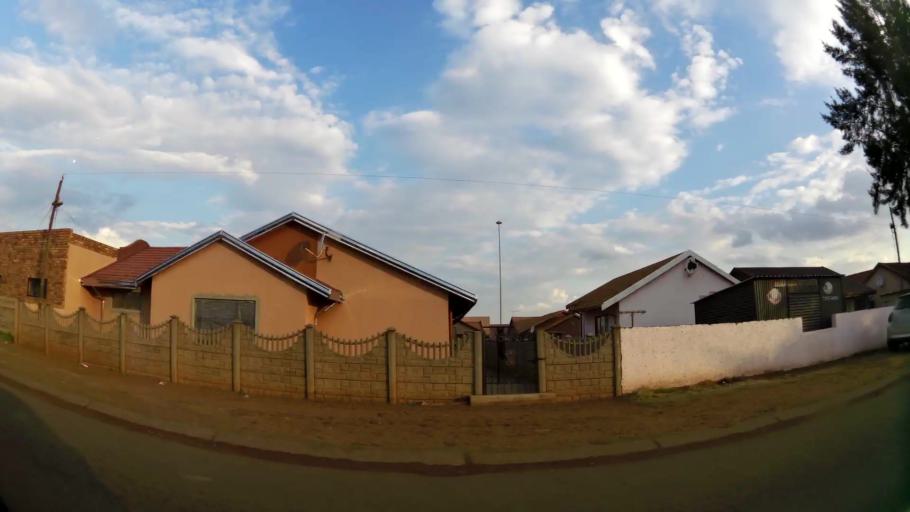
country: ZA
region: Gauteng
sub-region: City of Johannesburg Metropolitan Municipality
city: Orange Farm
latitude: -26.5937
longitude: 27.8335
